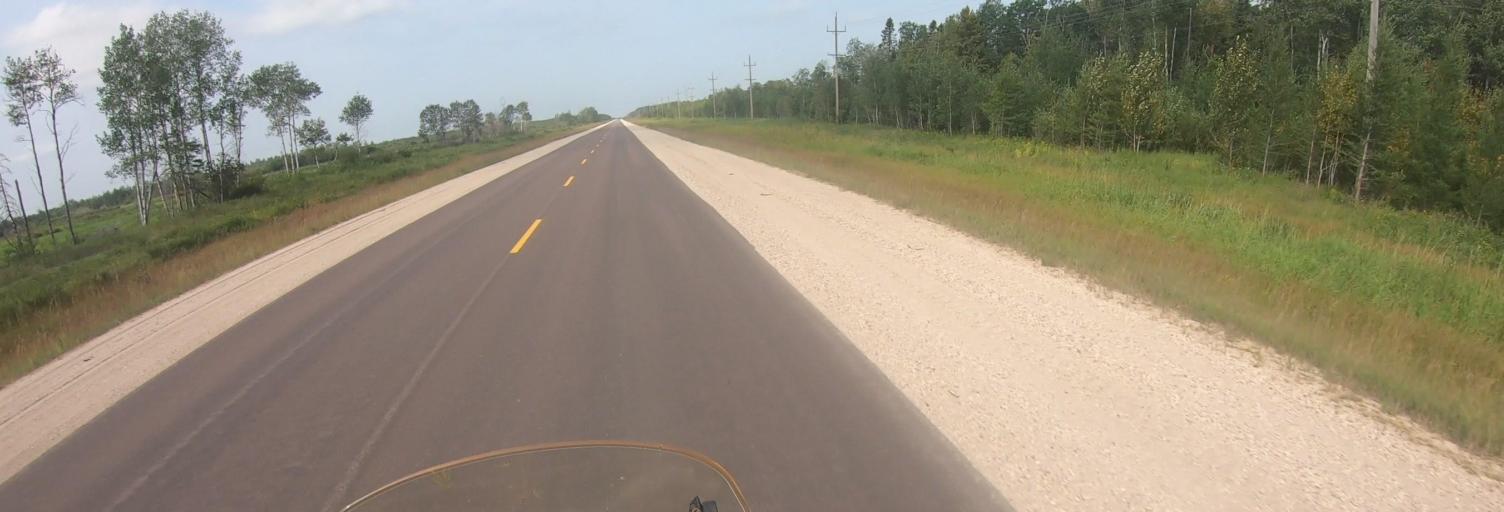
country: CA
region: Manitoba
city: La Broquerie
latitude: 49.2670
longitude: -96.4017
